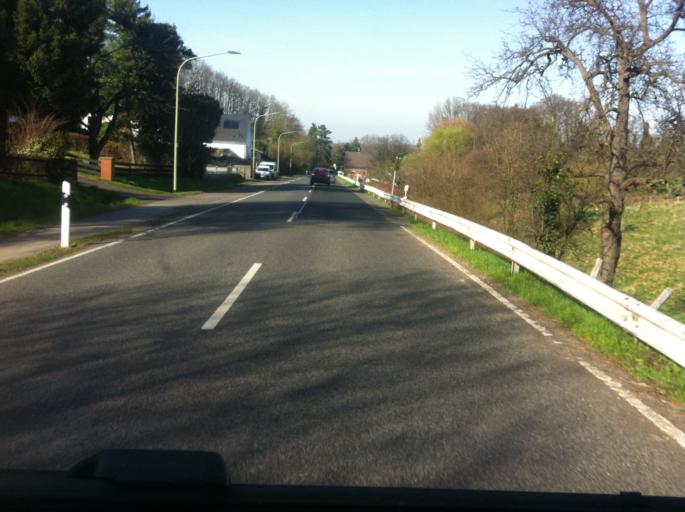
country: DE
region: North Rhine-Westphalia
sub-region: Regierungsbezirk Koln
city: Kreuzau
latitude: 50.7230
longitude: 6.4762
